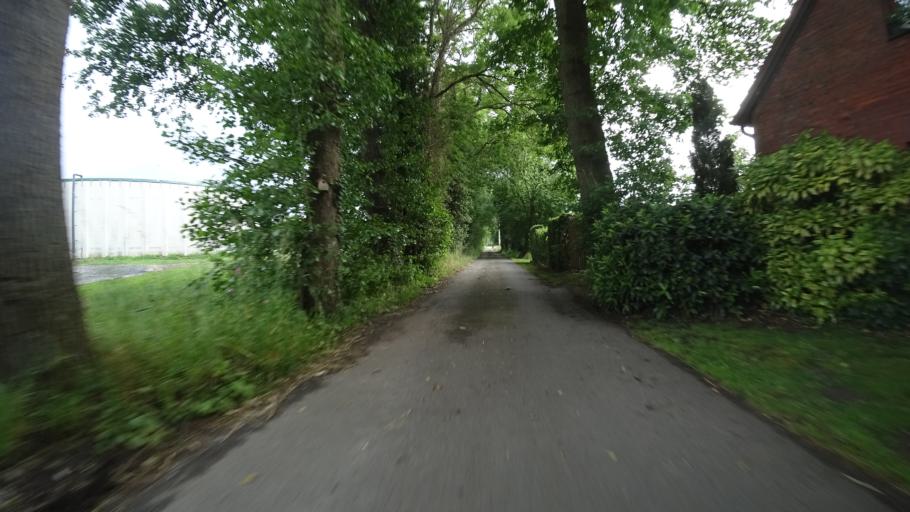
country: DE
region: North Rhine-Westphalia
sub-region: Regierungsbezirk Detmold
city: Guetersloh
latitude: 51.9455
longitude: 8.3762
